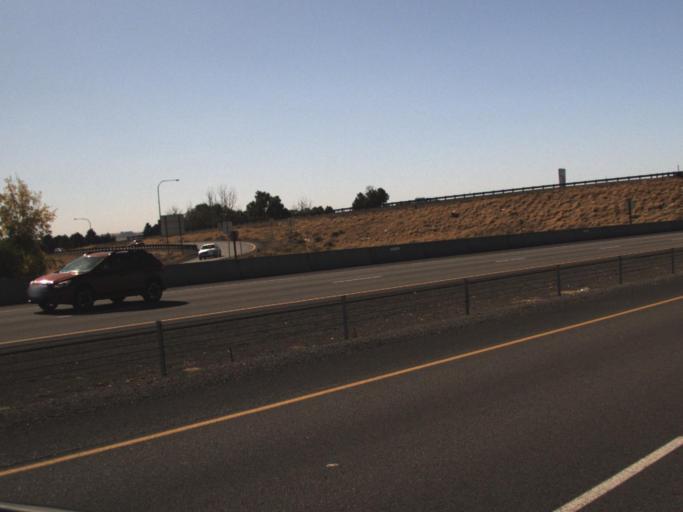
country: US
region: Washington
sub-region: Franklin County
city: Pasco
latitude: 46.2489
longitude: -119.1243
